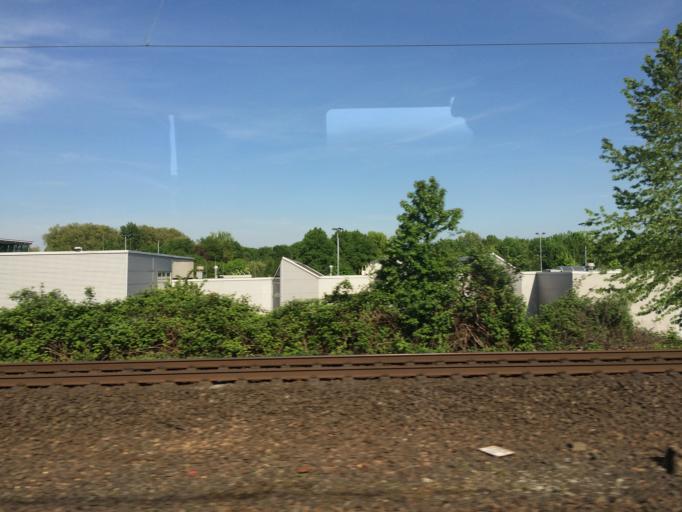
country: DE
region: North Rhine-Westphalia
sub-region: Regierungsbezirk Koln
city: Leverkusen
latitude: 51.0224
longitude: 6.9938
